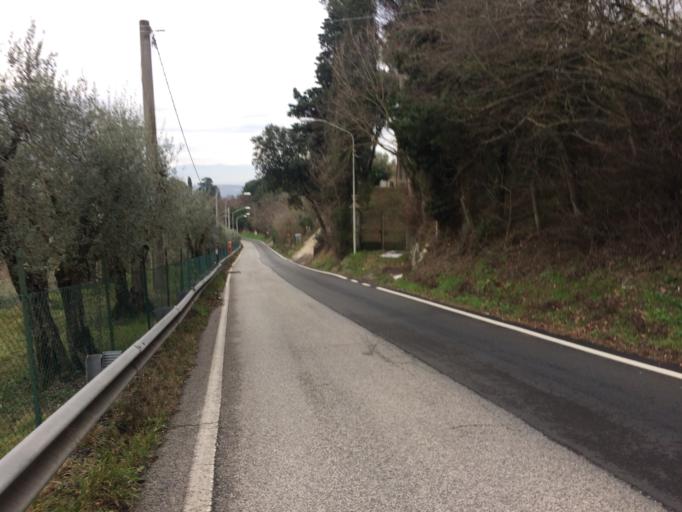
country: IT
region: Umbria
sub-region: Provincia di Perugia
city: Perugia
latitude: 43.1034
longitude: 12.3999
